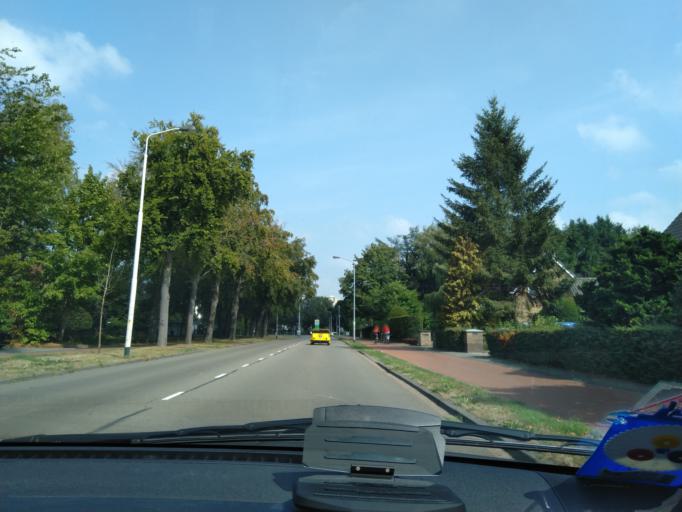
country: NL
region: North Brabant
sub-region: Gemeente Breda
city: Hoge Vucht
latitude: 51.5828
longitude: 4.8154
